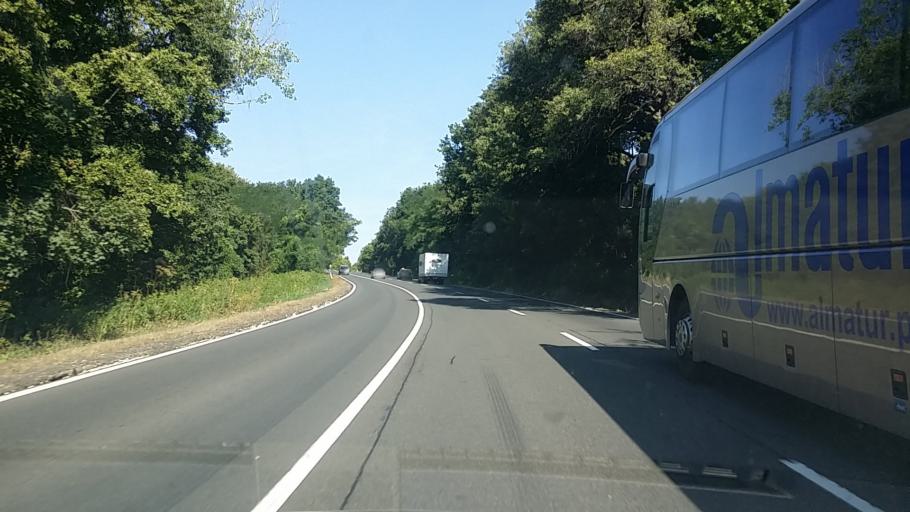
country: HU
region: Nograd
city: Retsag
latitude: 47.8700
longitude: 19.1094
